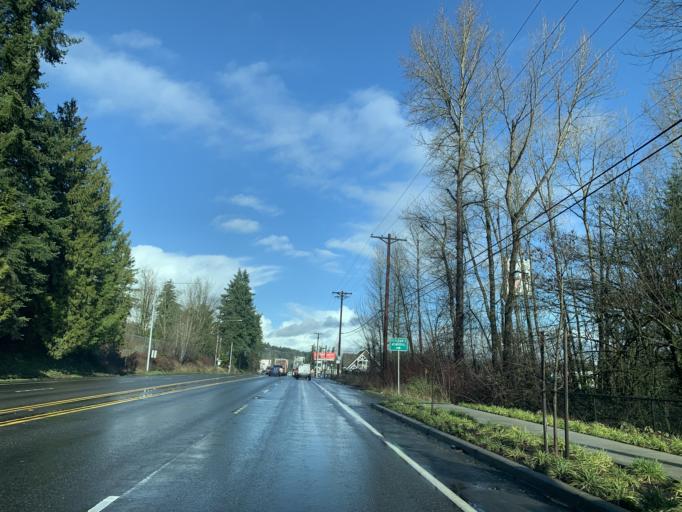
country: US
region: Washington
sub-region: Pierce County
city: Fife Heights
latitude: 47.2498
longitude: -122.3351
